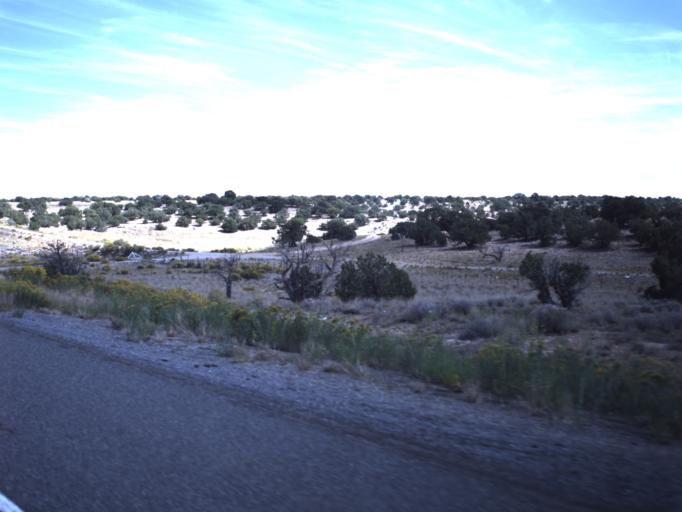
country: US
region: Utah
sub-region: Emery County
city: Castle Dale
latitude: 38.8964
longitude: -110.6020
